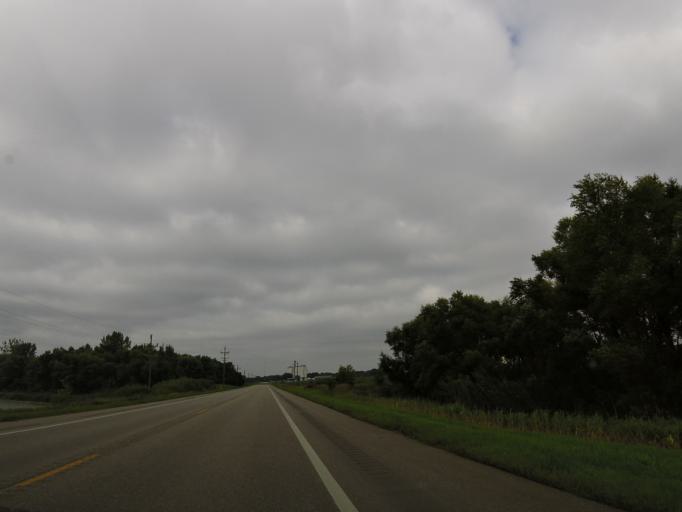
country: US
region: Minnesota
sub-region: Chippewa County
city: Montevideo
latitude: 44.9078
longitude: -95.6887
